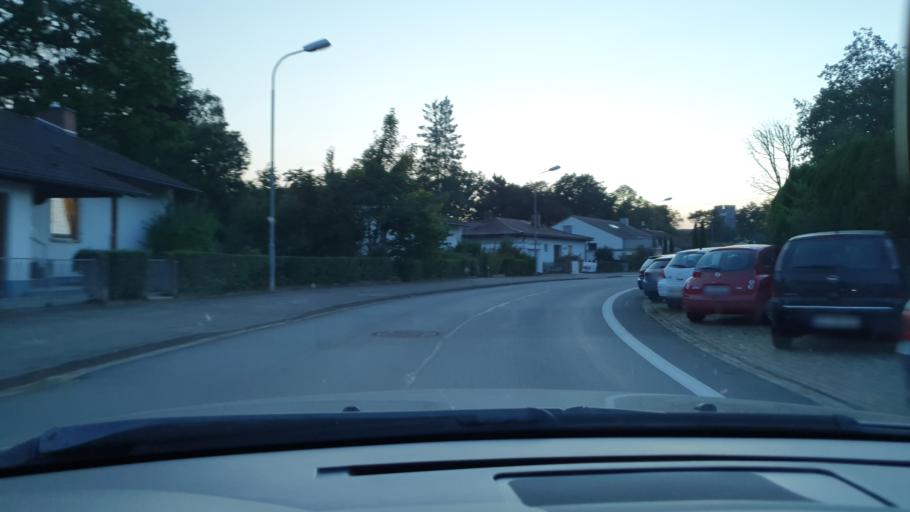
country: DE
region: Rheinland-Pfalz
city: Kaiserslautern
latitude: 49.4325
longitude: 7.7356
